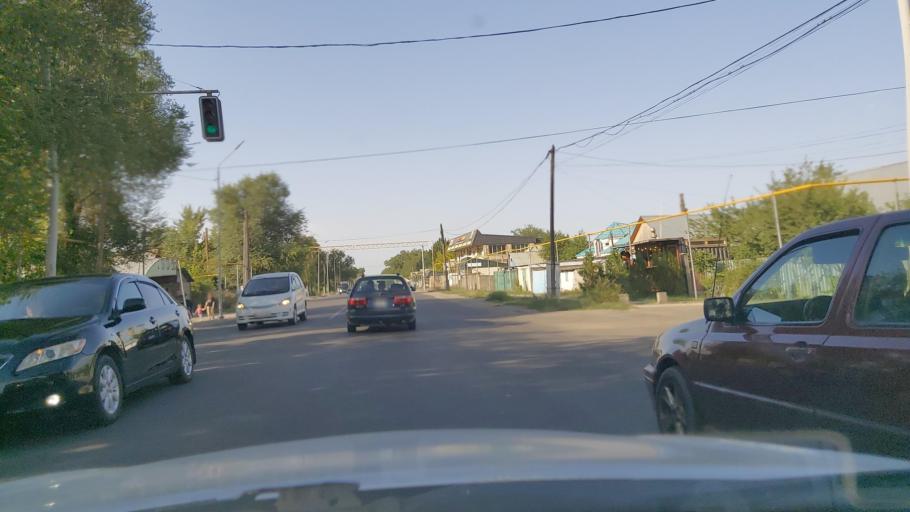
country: KZ
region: Almaty Oblysy
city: Energeticheskiy
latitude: 43.4993
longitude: 77.0414
